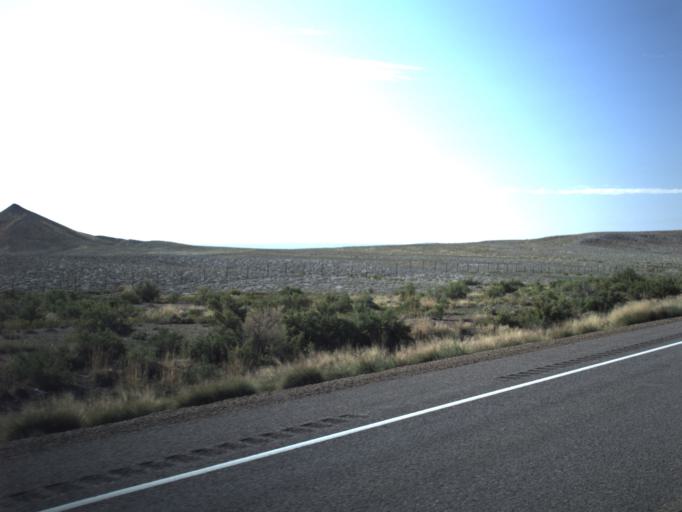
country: US
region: Utah
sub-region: Carbon County
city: Wellington
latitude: 39.4503
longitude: -110.8628
